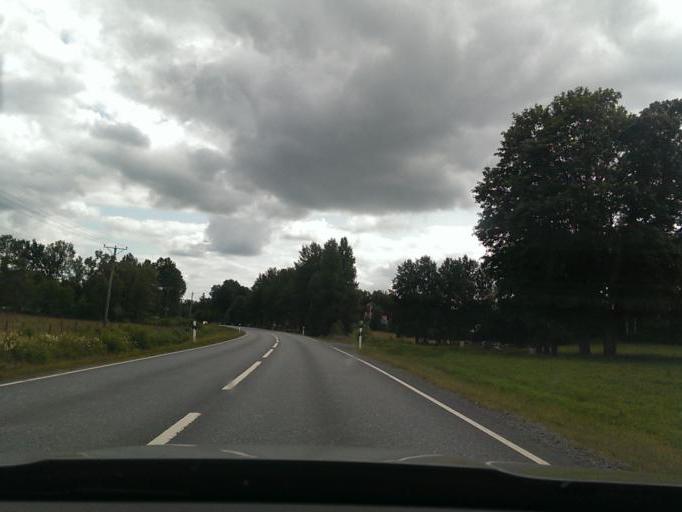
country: SE
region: Joenkoeping
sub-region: Varnamo Kommun
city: Varnamo
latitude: 57.2284
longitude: 14.0067
